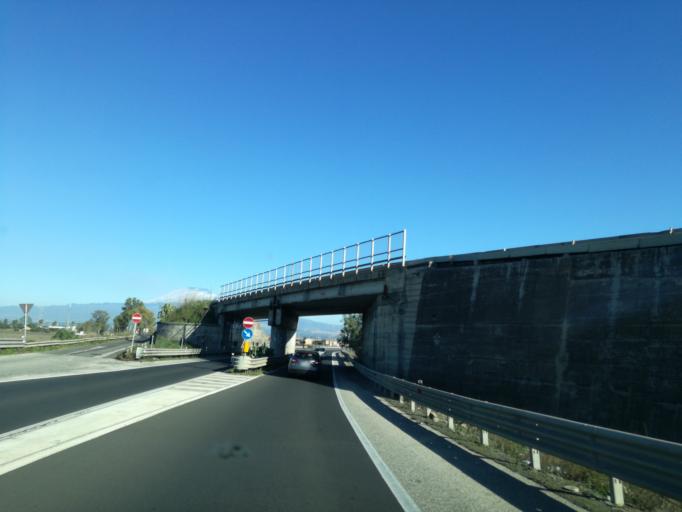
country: IT
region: Sicily
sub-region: Catania
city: Motta Sant'Anastasia
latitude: 37.4151
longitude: 14.9076
